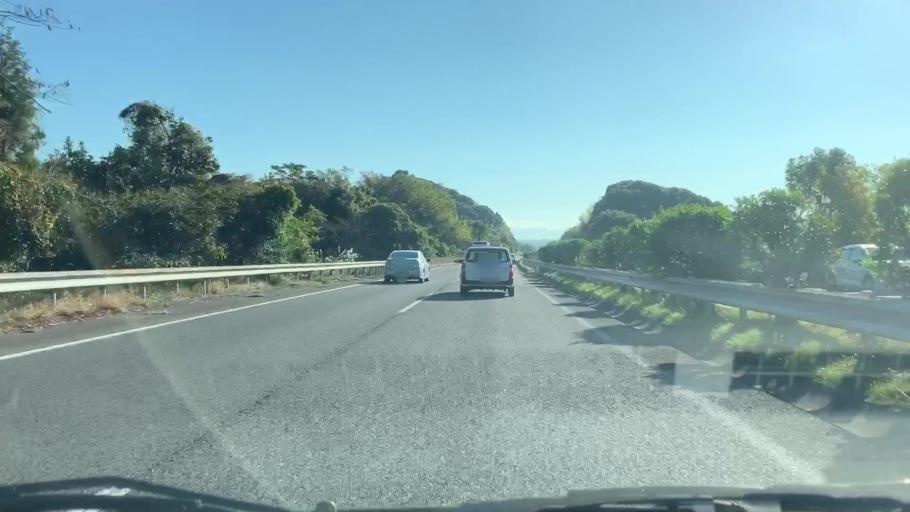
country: JP
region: Saga Prefecture
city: Saga-shi
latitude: 33.3101
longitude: 130.2197
